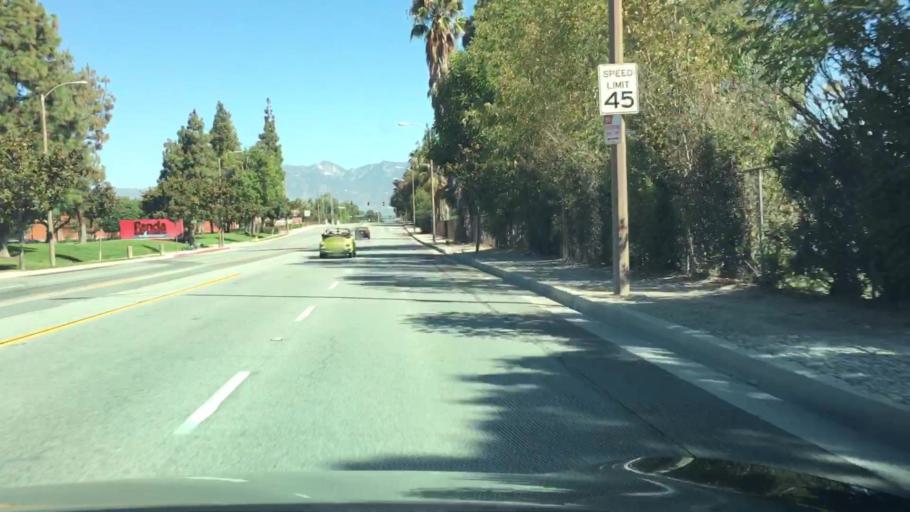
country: US
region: California
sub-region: Los Angeles County
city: South San Gabriel
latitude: 34.0479
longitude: -118.0818
